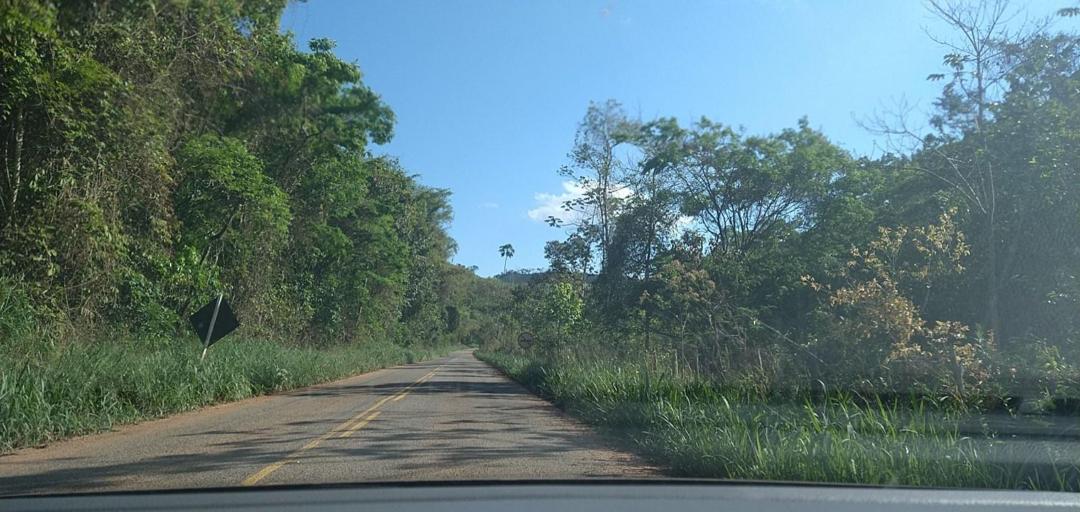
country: BR
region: Minas Gerais
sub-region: Alvinopolis
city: Alvinopolis
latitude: -20.1781
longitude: -42.9308
